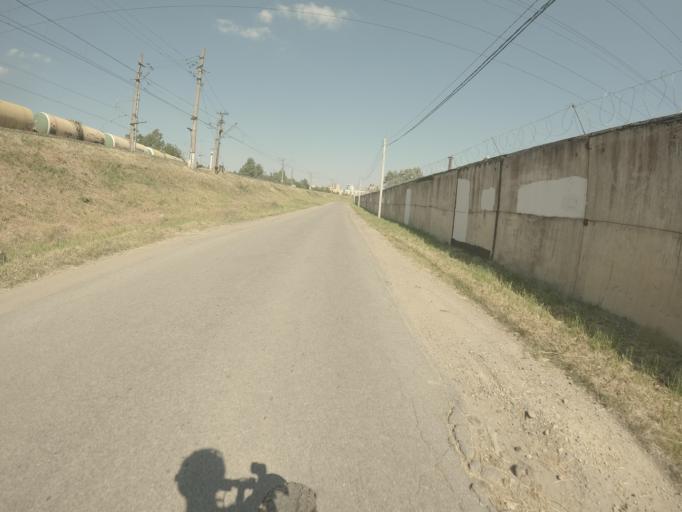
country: RU
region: Leningrad
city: Rybatskoye
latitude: 59.8359
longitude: 30.4752
